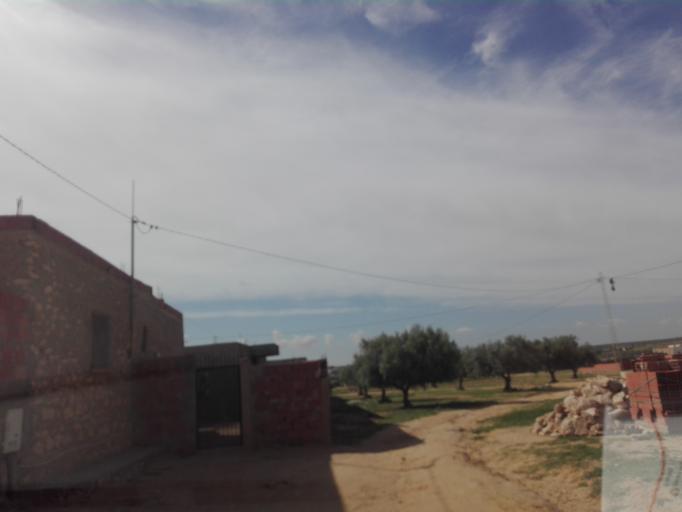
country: TN
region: Safaqis
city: Sfax
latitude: 34.7416
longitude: 10.5127
